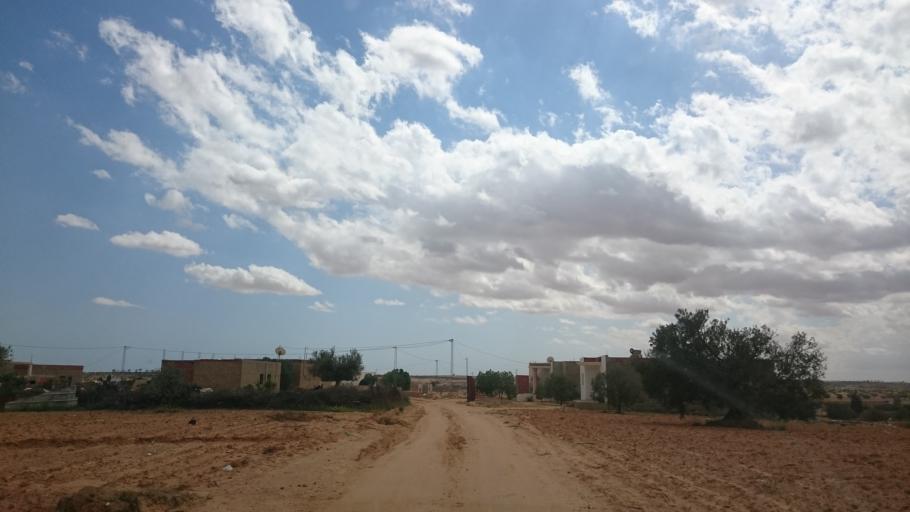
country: TN
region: Safaqis
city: Sfax
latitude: 34.7481
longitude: 10.4861
